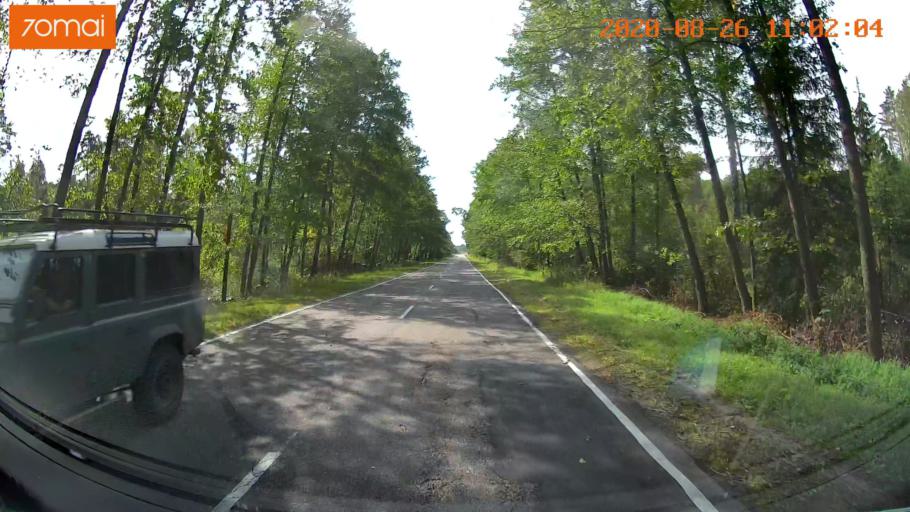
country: RU
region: Rjazan
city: Izhevskoye
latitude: 54.5555
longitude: 41.2262
